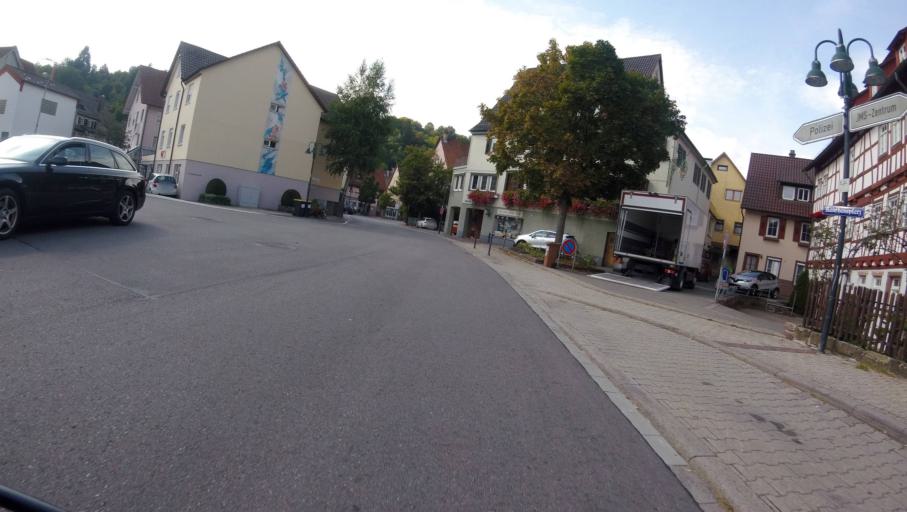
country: DE
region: Baden-Wuerttemberg
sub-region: Karlsruhe Region
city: Altensteig
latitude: 48.5847
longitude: 8.6043
